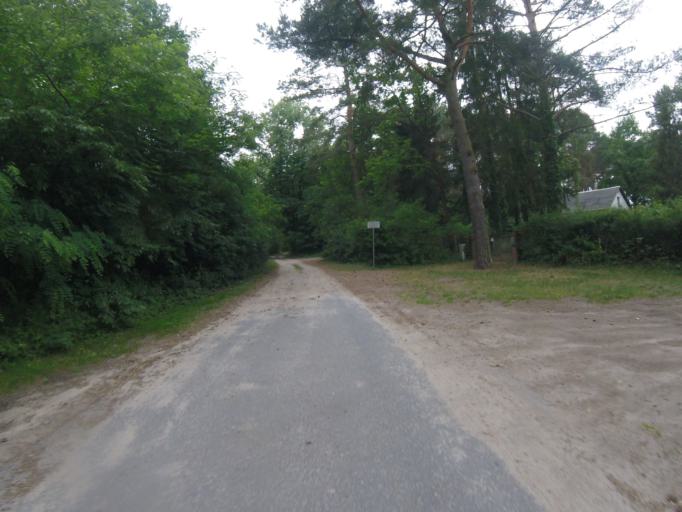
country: DE
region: Brandenburg
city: Bestensee
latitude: 52.2307
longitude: 13.6271
